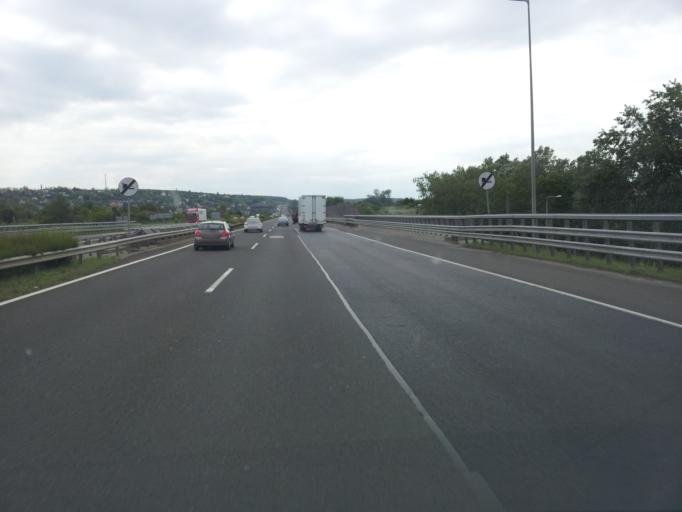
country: HU
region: Pest
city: Szada
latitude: 47.6144
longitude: 19.3326
